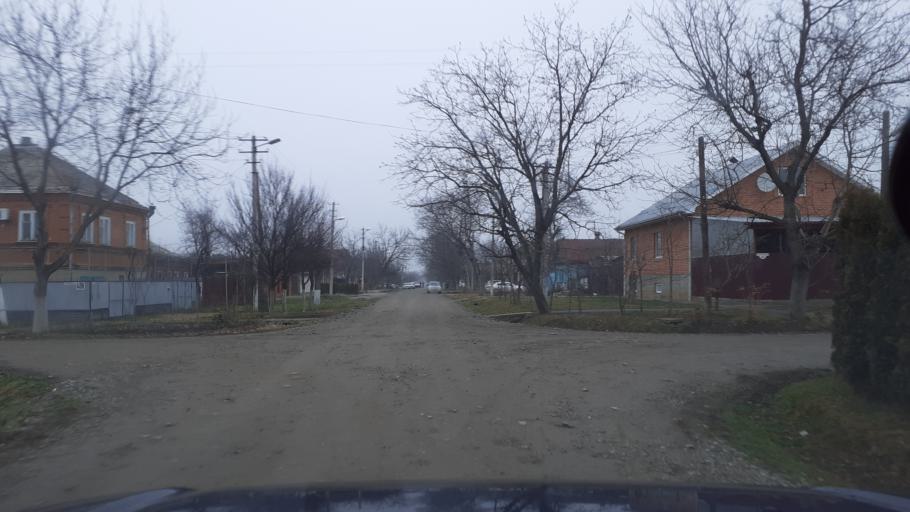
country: RU
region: Adygeya
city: Maykop
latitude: 44.6160
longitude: 40.0876
